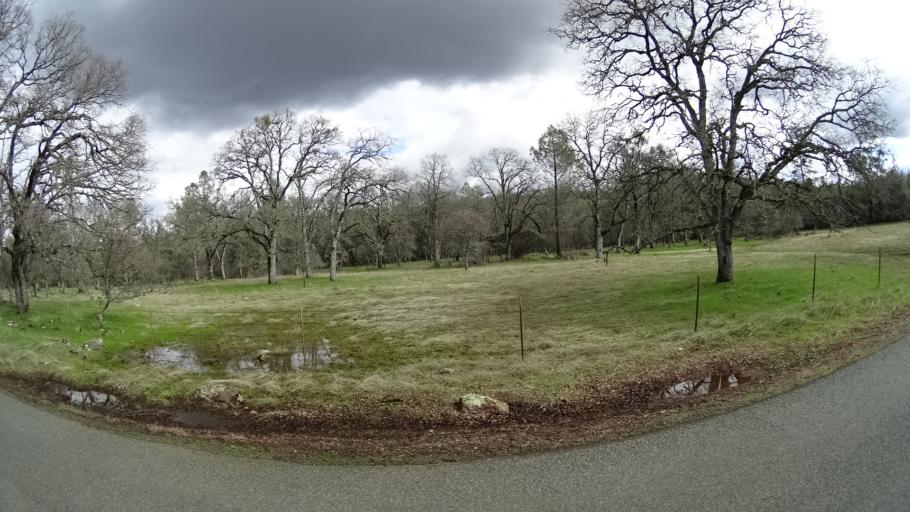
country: US
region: California
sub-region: Butte County
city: Oroville
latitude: 39.6216
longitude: -121.5278
